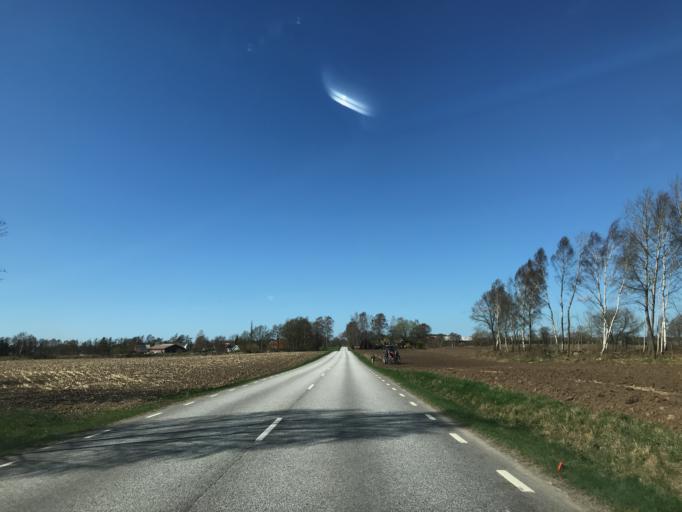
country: SE
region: Skane
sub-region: Klippans Kommun
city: Ljungbyhed
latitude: 56.0572
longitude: 13.2350
